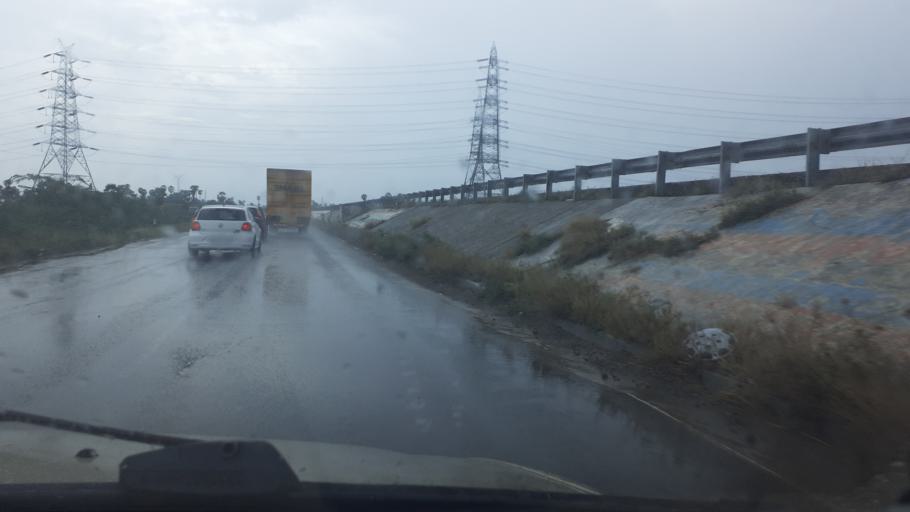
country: IN
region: Tamil Nadu
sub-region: Thoothukkudi
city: Kayattar
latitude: 8.9298
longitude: 77.7690
